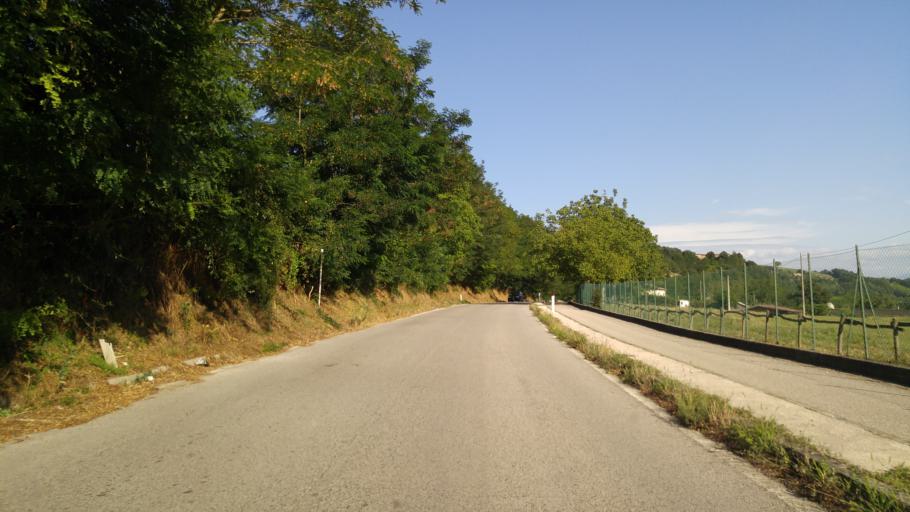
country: IT
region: The Marches
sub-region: Provincia di Pesaro e Urbino
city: Urbania
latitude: 43.6826
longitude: 12.5177
